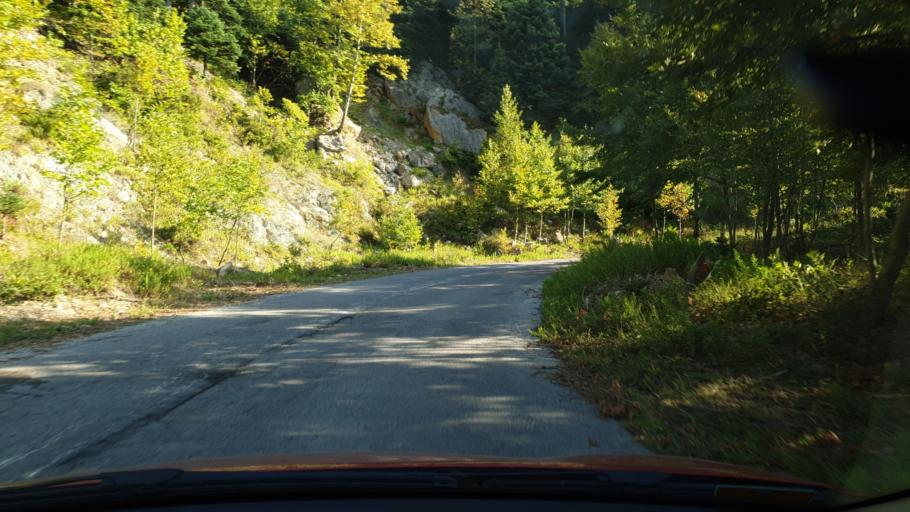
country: GR
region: Central Greece
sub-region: Nomos Evvoias
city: Yimnon
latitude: 38.6057
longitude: 23.9210
